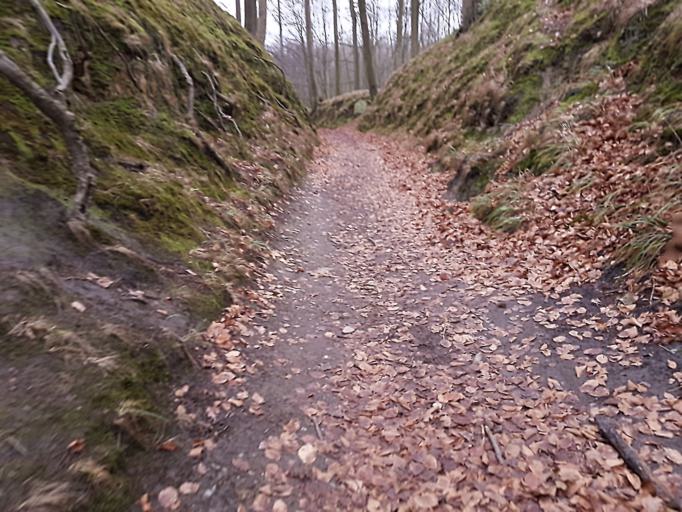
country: DE
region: Mecklenburg-Vorpommern
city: Ostseebad Binz
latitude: 54.3987
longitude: 13.6327
